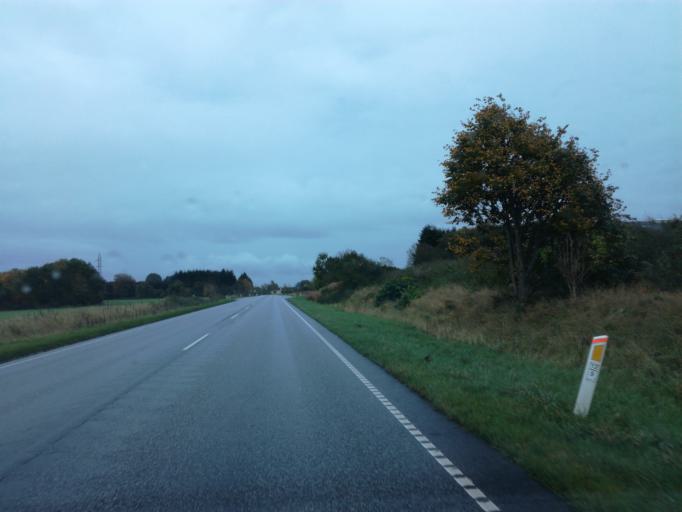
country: DK
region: South Denmark
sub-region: Vejle Kommune
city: Brejning
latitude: 55.6374
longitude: 9.6770
